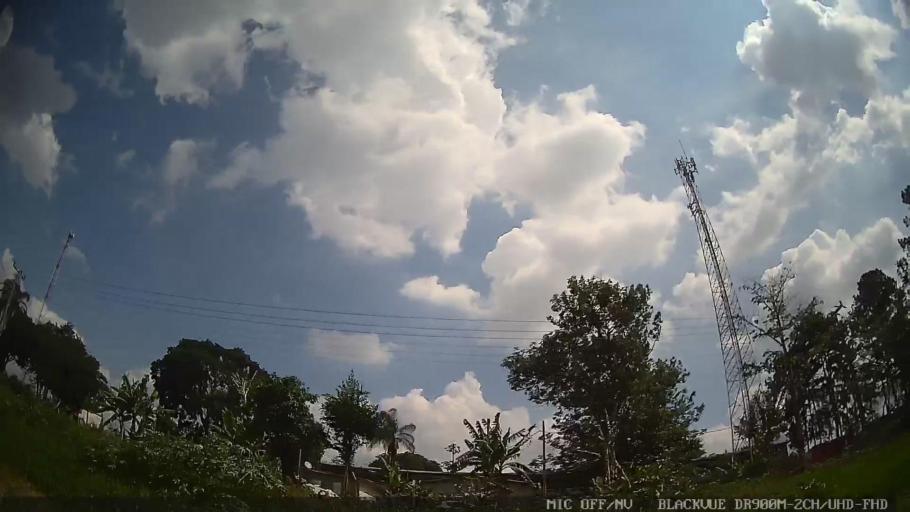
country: BR
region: Sao Paulo
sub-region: Braganca Paulista
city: Braganca Paulista
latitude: -22.9435
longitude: -46.6610
